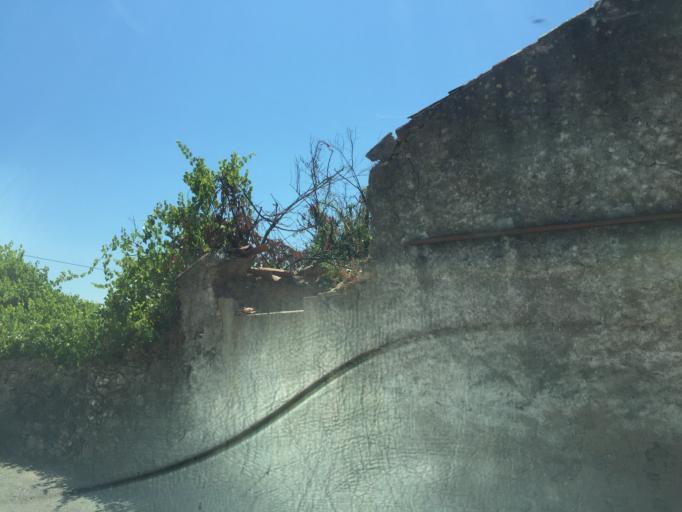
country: PT
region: Santarem
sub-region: Tomar
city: Tomar
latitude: 39.5757
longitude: -8.3009
